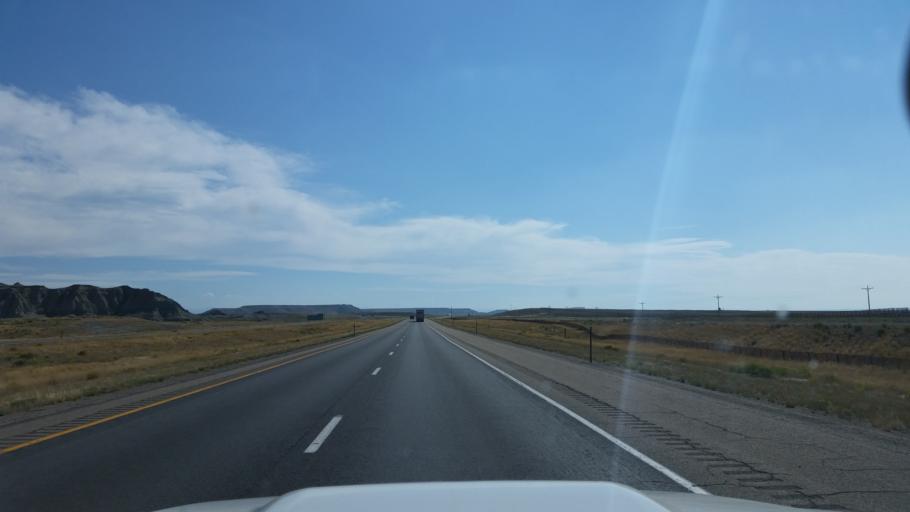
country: US
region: Wyoming
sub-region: Uinta County
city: Lyman
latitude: 41.4766
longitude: -110.0329
